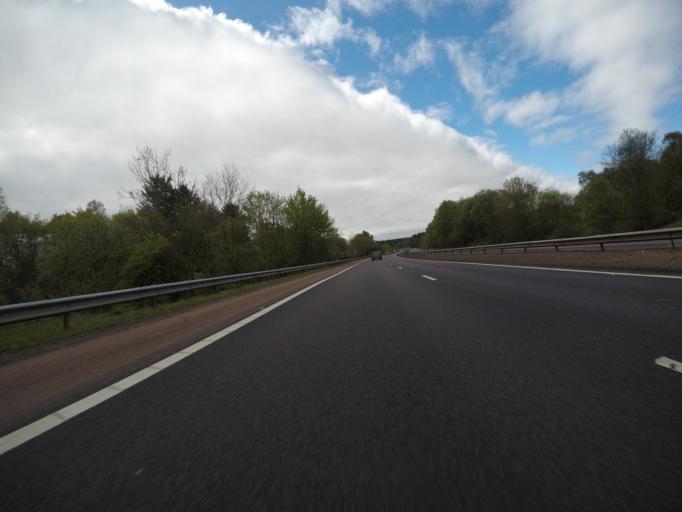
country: GB
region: Scotland
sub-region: Fife
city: Kelty
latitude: 56.1447
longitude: -3.3934
